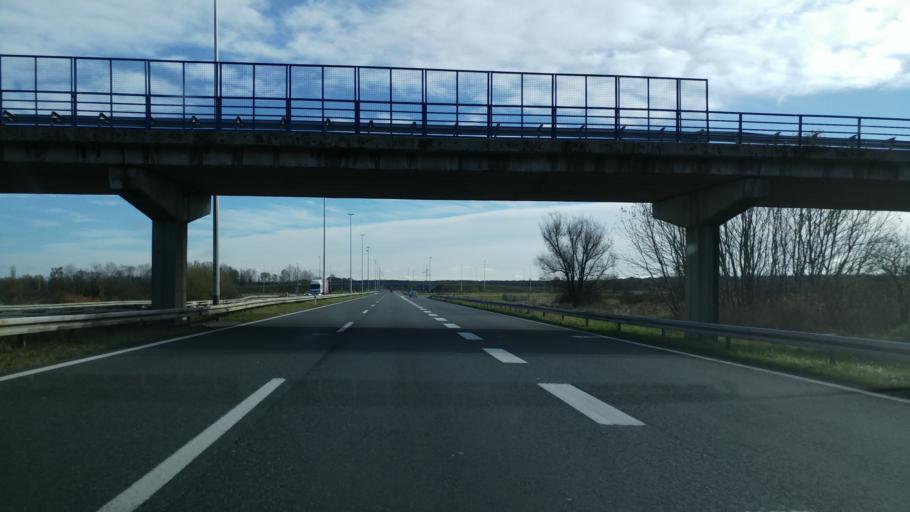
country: HR
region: Sisacko-Moslavacka
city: Kutina
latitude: 45.4615
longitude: 16.7565
